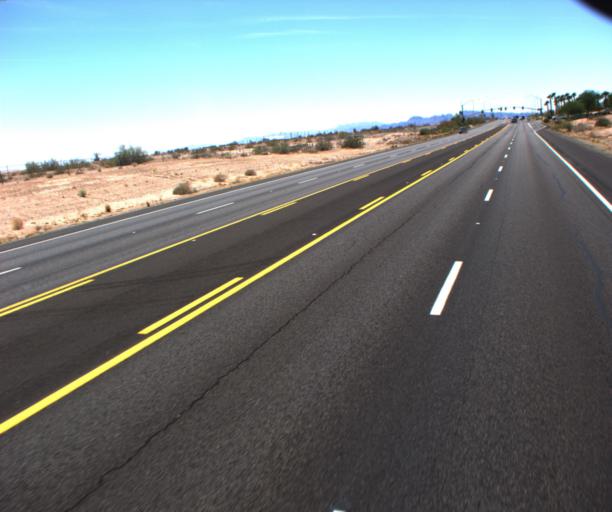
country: US
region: Arizona
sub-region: La Paz County
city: Parker
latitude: 34.1610
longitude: -114.2641
